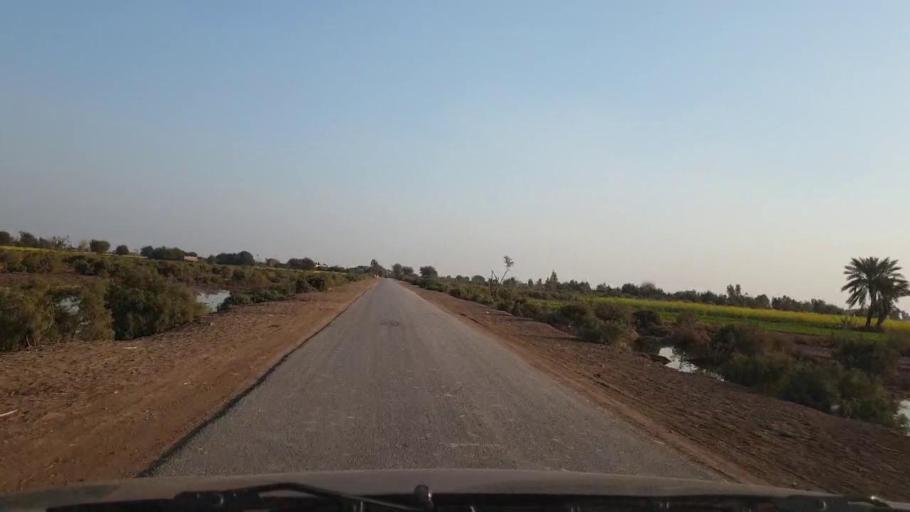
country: PK
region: Sindh
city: Jhol
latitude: 25.9335
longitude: 68.9161
